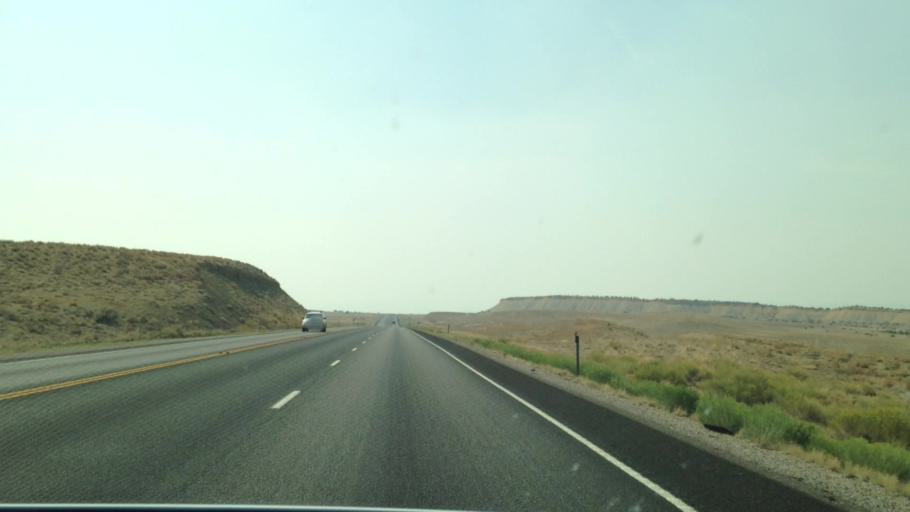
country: US
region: Utah
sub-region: Carbon County
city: Wellington
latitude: 39.5380
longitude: -110.6054
